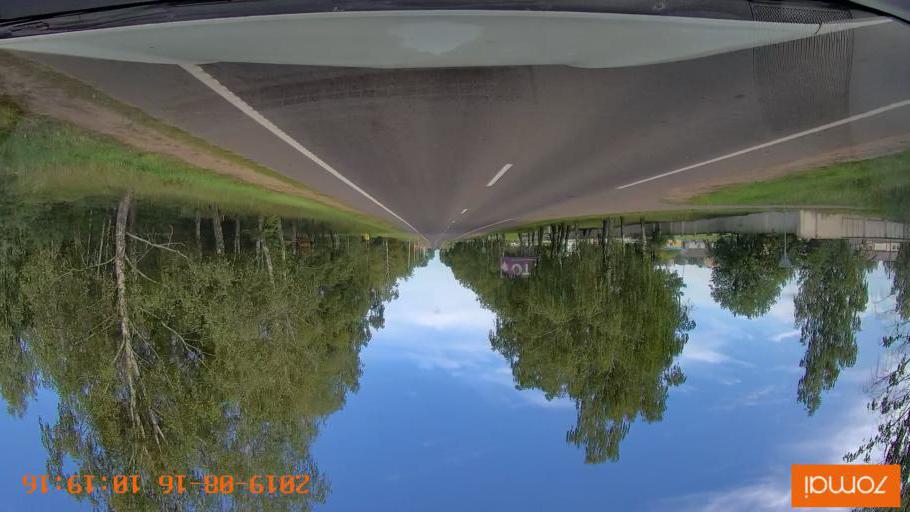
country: BY
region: Mogilev
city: Asipovichy
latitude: 53.3063
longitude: 28.6701
